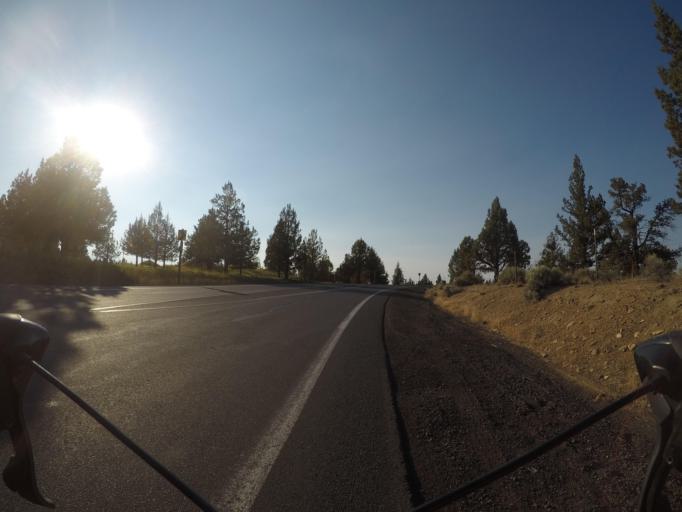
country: US
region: Oregon
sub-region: Deschutes County
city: Redmond
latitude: 44.2740
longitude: -121.2624
